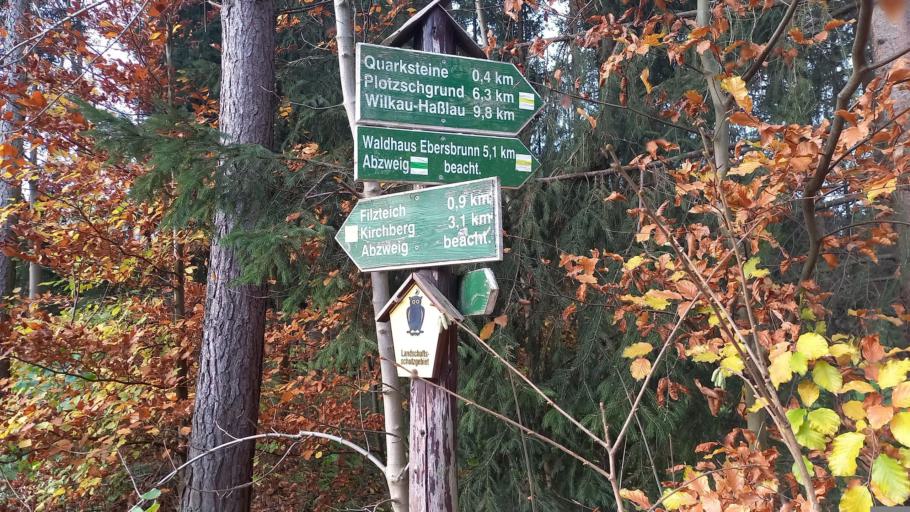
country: DE
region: Saxony
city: Hirschfeld
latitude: 50.6339
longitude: 12.4921
